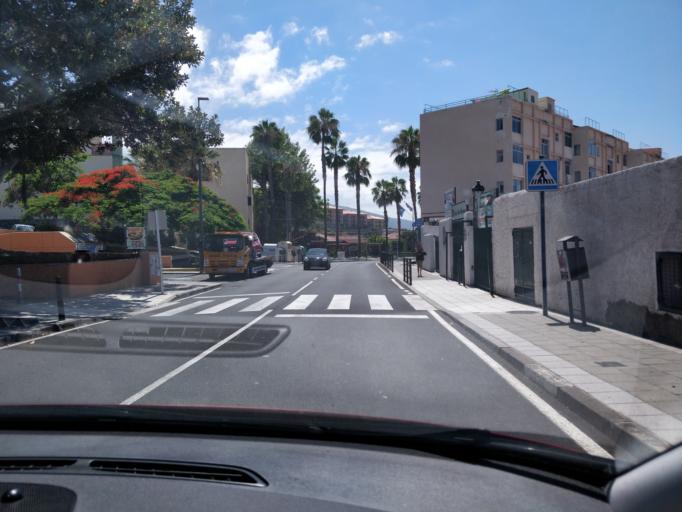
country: ES
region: Canary Islands
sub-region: Provincia de Santa Cruz de Tenerife
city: Puerto de la Cruz
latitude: 28.4104
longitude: -16.5534
